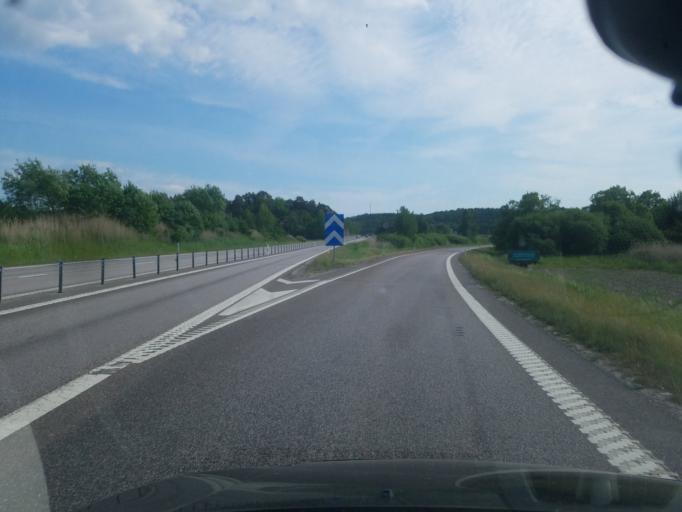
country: SE
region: Halland
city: Saro
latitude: 57.5251
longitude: 11.9680
